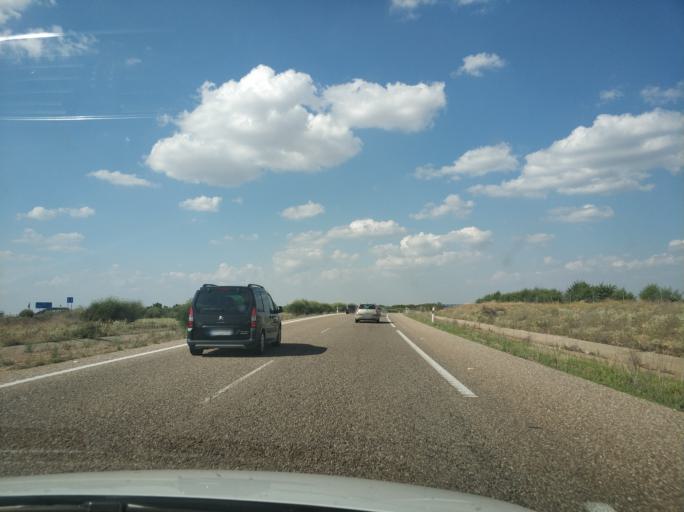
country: ES
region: Castille and Leon
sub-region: Provincia de Zamora
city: San Cristobal de Entrevinas
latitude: 42.0560
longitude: -5.6751
